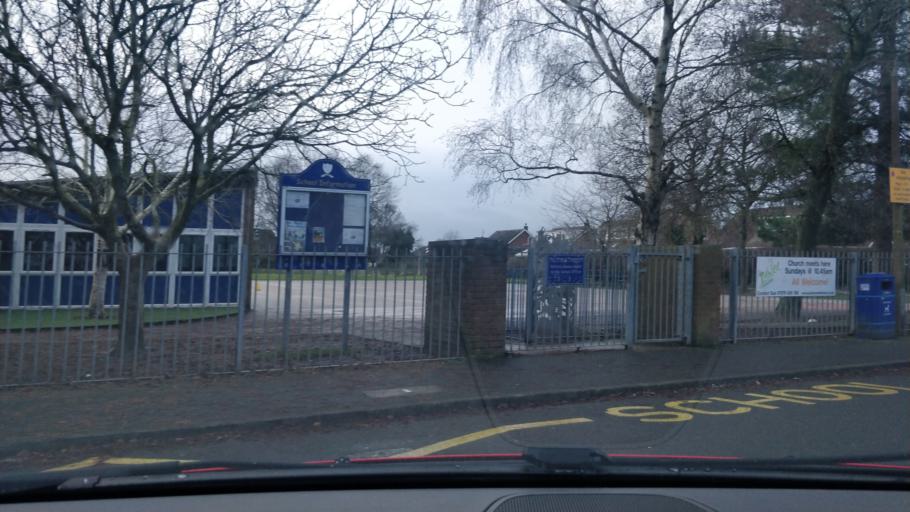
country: GB
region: England
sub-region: Lancashire
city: Preston
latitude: 53.7425
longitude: -2.7388
